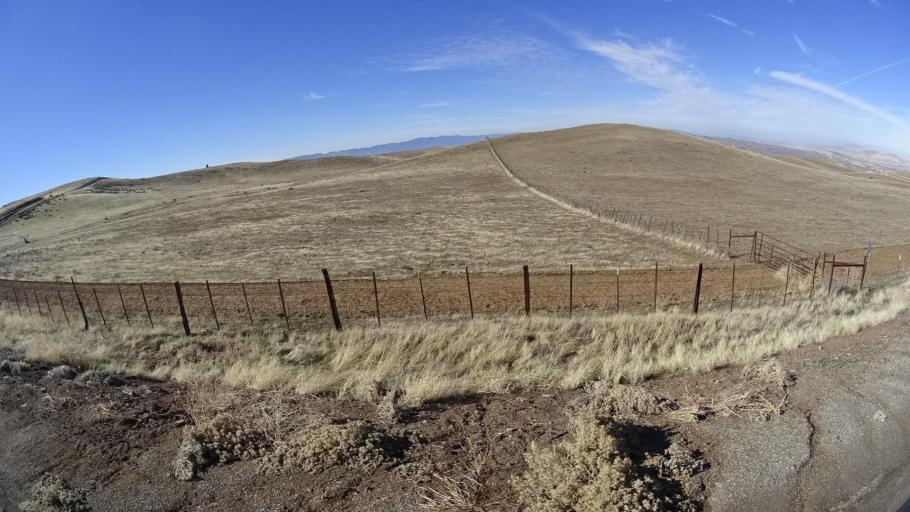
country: US
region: California
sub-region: Kern County
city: Maricopa
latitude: 34.9243
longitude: -119.4096
